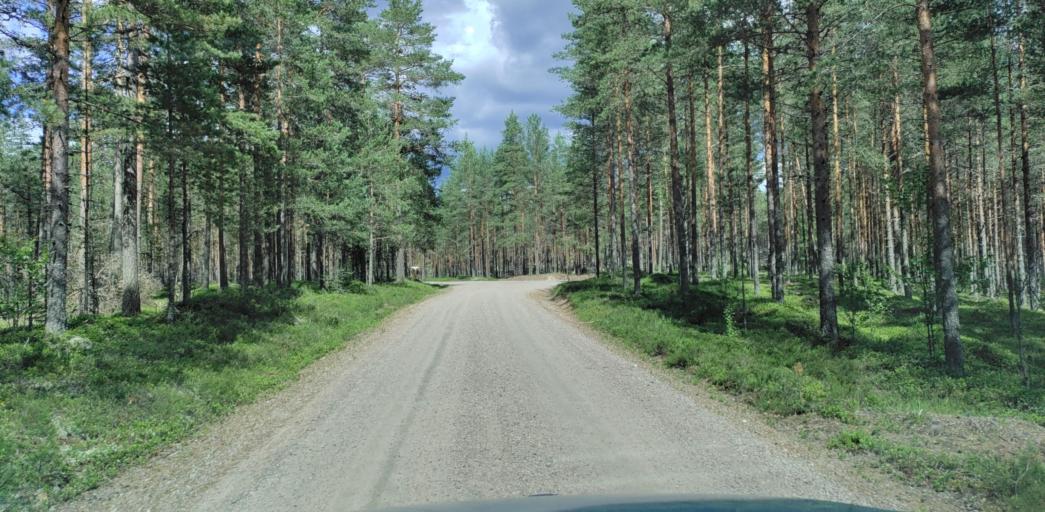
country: SE
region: Vaermland
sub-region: Hagfors Kommun
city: Ekshaerad
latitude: 60.0602
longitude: 13.2888
